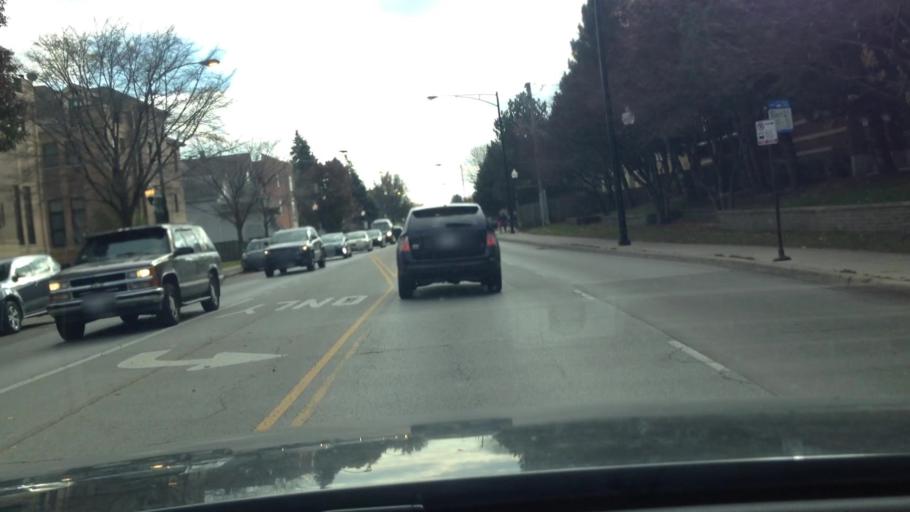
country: US
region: Illinois
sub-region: Cook County
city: Harwood Heights
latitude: 41.9564
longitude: -87.7867
